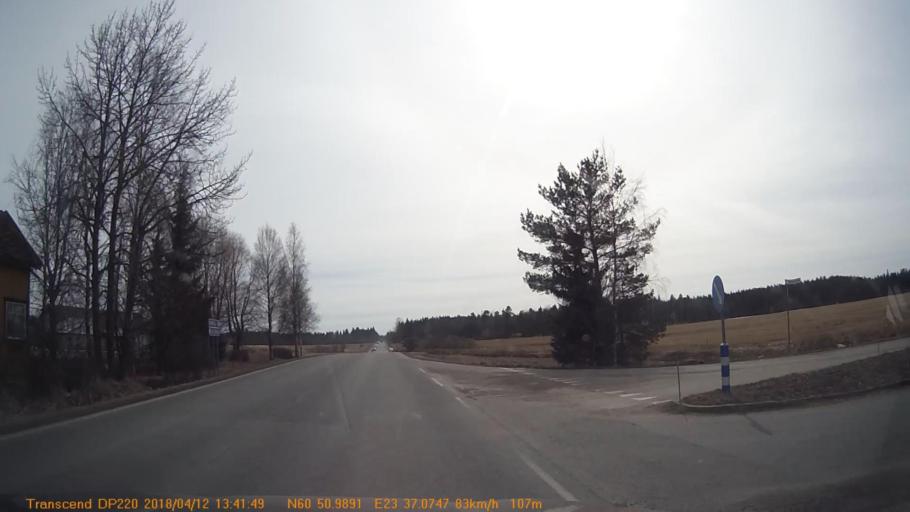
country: FI
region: Haeme
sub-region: Forssa
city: Forssa
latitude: 60.8490
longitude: 23.6179
